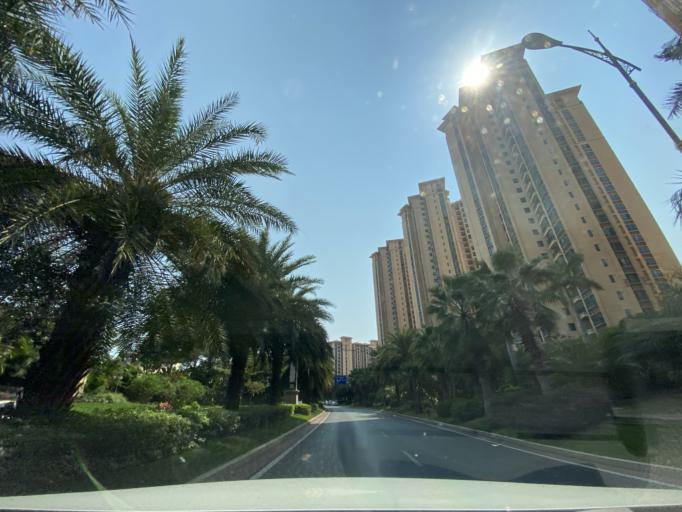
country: CN
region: Hainan
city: Yingzhou
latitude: 18.3961
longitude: 109.8405
